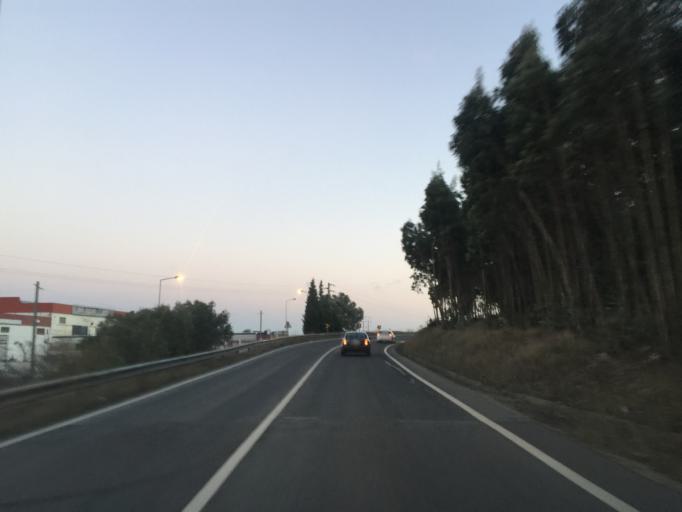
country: PT
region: Lisbon
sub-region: Alenquer
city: Alenquer
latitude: 39.1282
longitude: -8.9923
